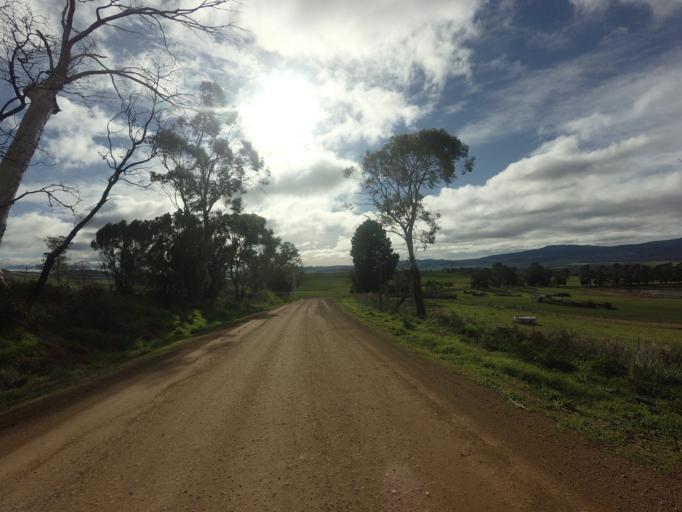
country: AU
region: Tasmania
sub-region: Derwent Valley
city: New Norfolk
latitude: -42.7196
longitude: 146.8740
